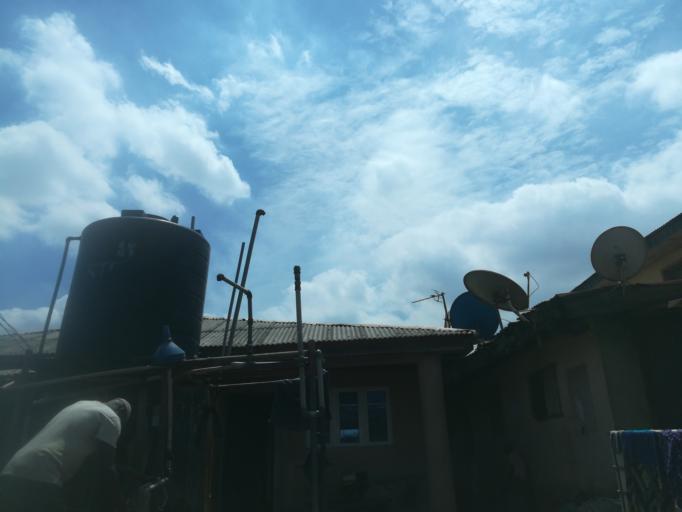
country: NG
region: Lagos
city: Oshodi
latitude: 6.5664
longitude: 3.3345
